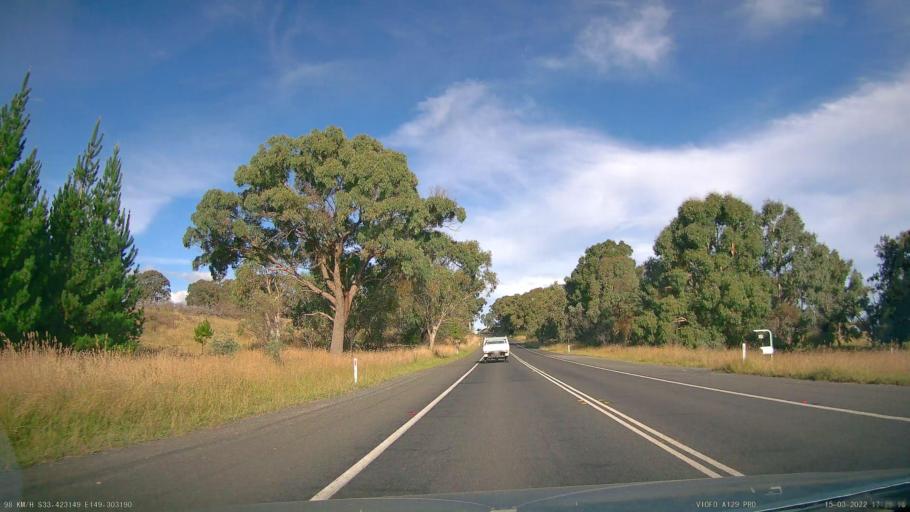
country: AU
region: New South Wales
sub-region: Blayney
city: Blayney
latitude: -33.4233
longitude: 149.3034
